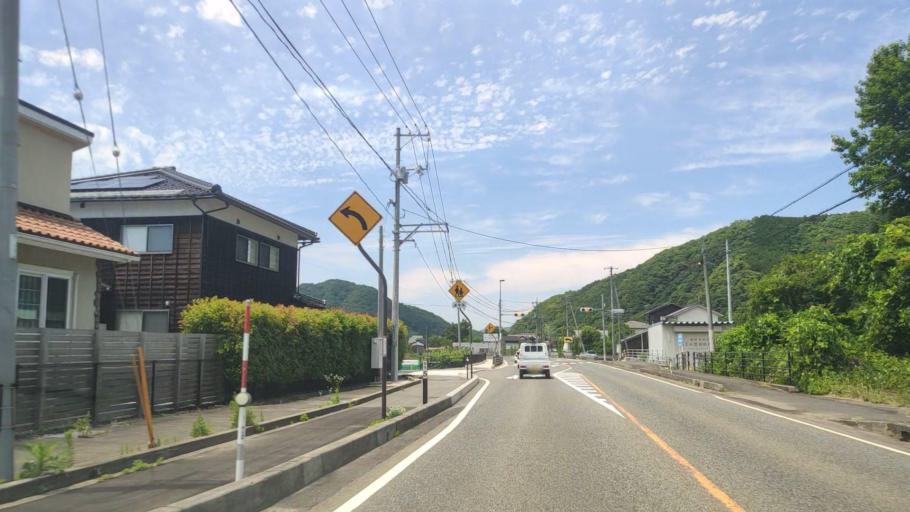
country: JP
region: Tottori
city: Tottori
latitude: 35.3747
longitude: 134.3036
